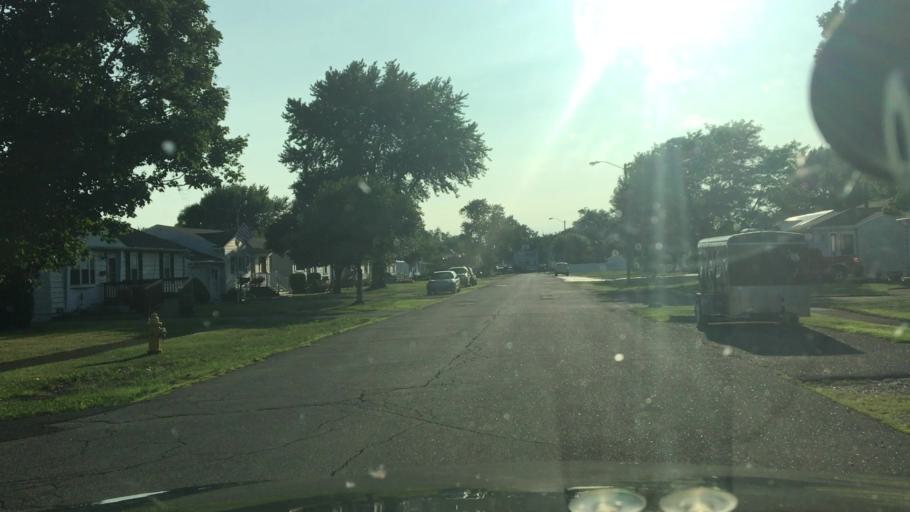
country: US
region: New York
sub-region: Erie County
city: Blasdell
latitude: 42.8005
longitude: -78.8209
